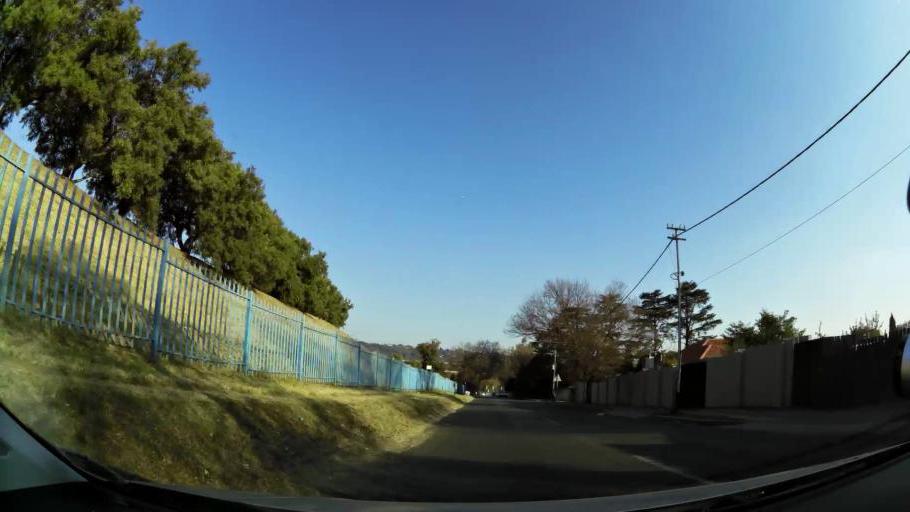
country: ZA
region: Gauteng
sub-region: City of Johannesburg Metropolitan Municipality
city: Johannesburg
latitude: -26.1469
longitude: 28.0814
